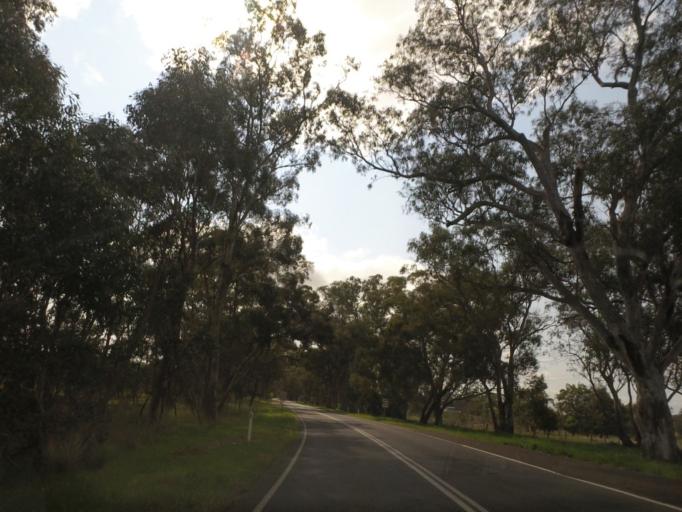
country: AU
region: Victoria
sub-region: Murrindindi
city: Kinglake West
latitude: -37.1068
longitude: 145.0945
